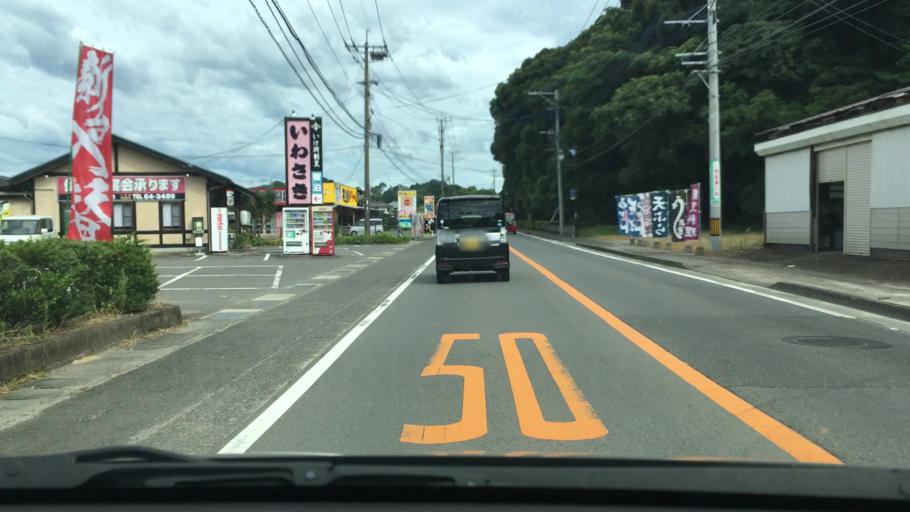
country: JP
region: Nagasaki
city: Togitsu
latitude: 32.8879
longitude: 129.7879
